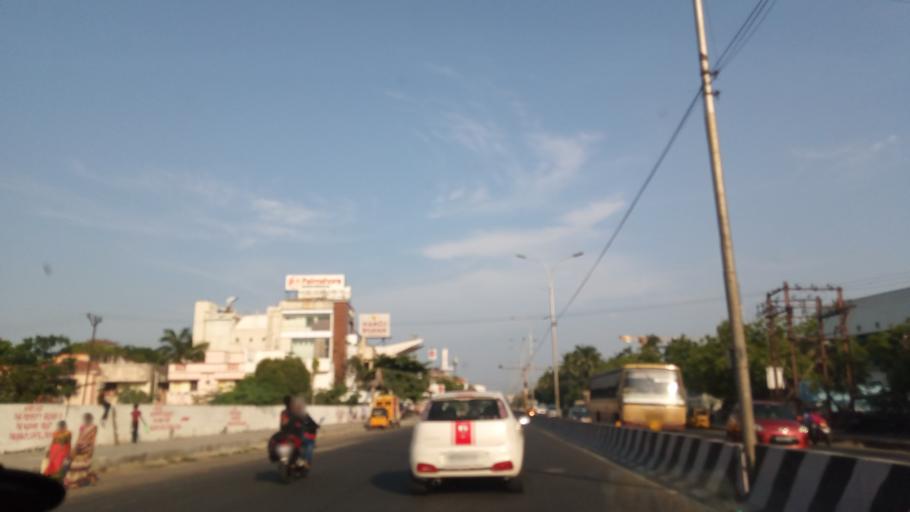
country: IN
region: Tamil Nadu
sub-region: Kancheepuram
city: Manappakkam
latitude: 13.0266
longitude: 80.1738
